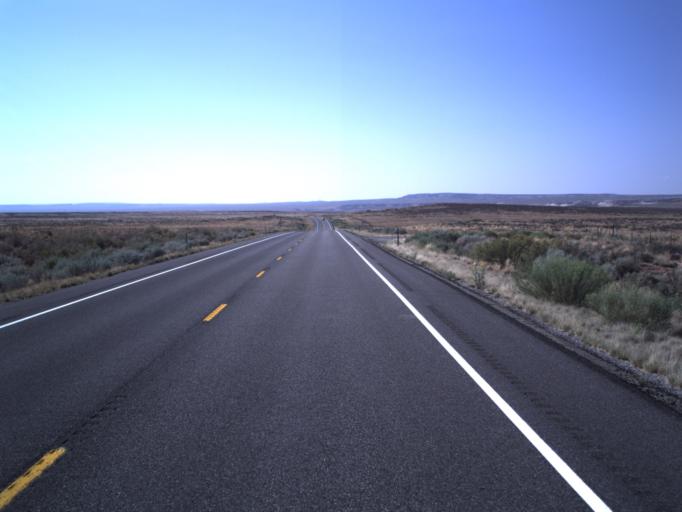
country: US
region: Utah
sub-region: San Juan County
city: Blanding
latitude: 37.3459
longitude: -109.5193
